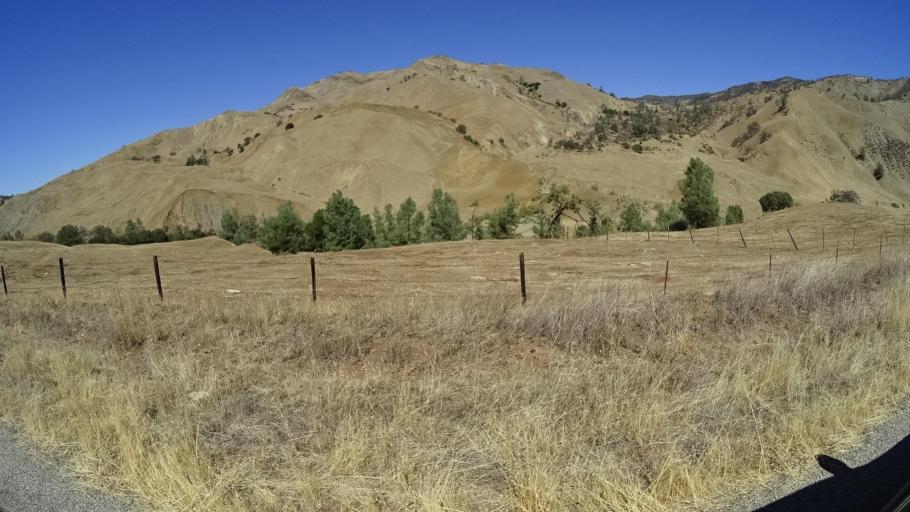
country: US
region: California
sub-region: Monterey County
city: King City
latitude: 36.2912
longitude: -120.8746
